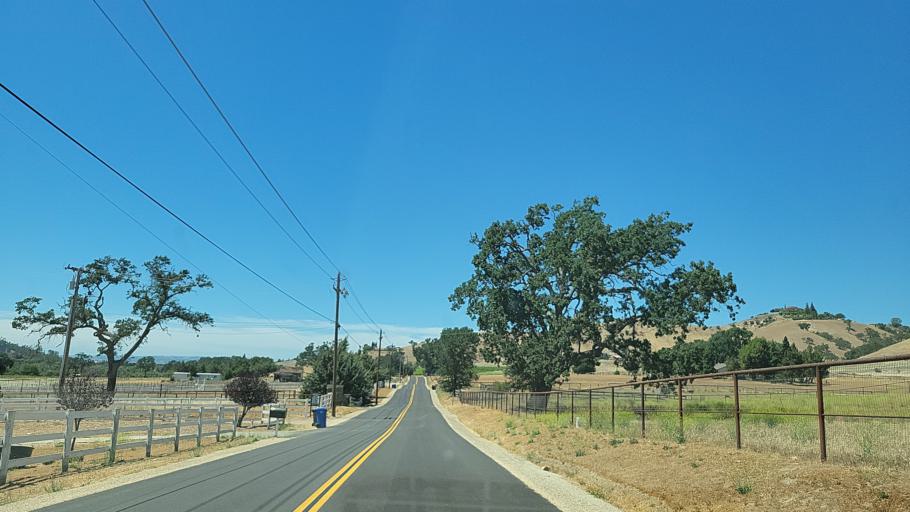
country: US
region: California
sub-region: San Luis Obispo County
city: Atascadero
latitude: 35.4822
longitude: -120.6309
